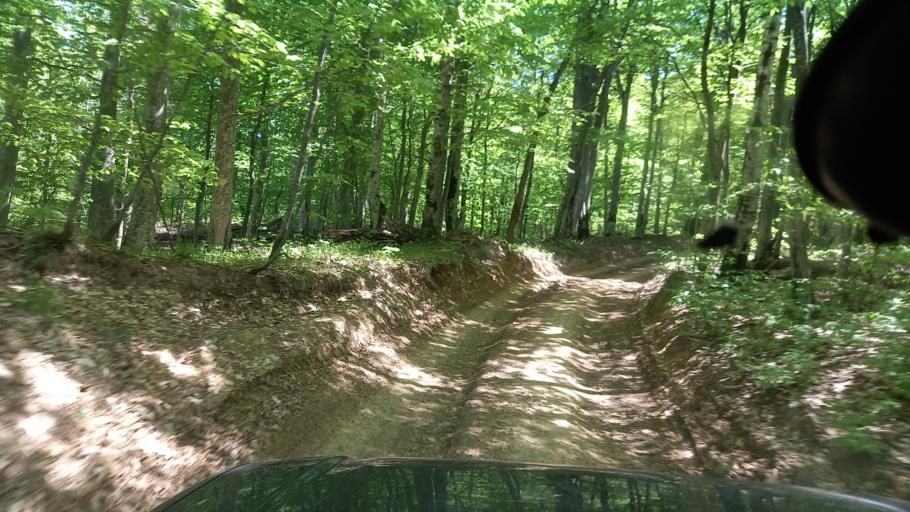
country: RU
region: Krasnodarskiy
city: Tuapse
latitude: 44.2553
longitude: 39.2852
